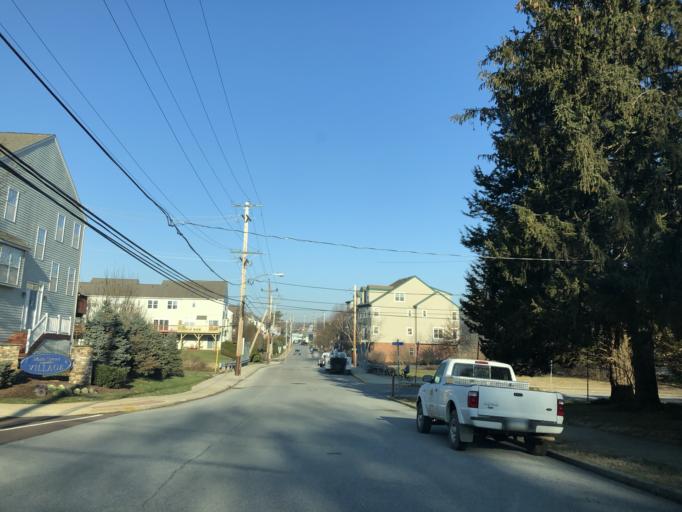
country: US
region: Pennsylvania
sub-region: Chester County
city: Downingtown
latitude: 40.0048
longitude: -75.6978
